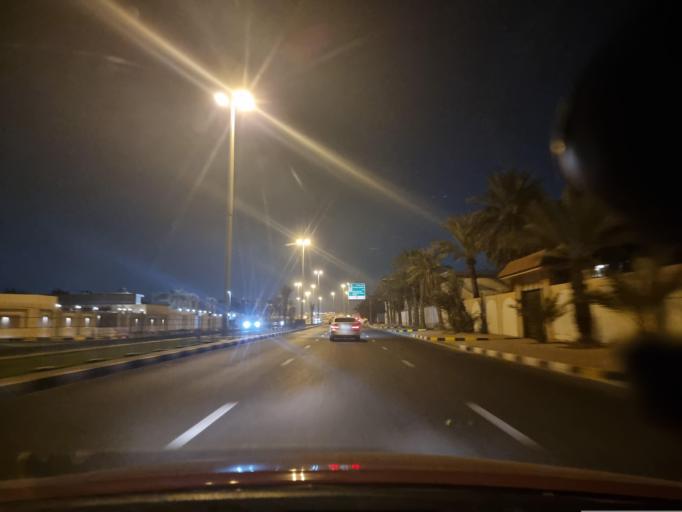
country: AE
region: Ash Shariqah
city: Sharjah
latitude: 25.3614
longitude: 55.4382
